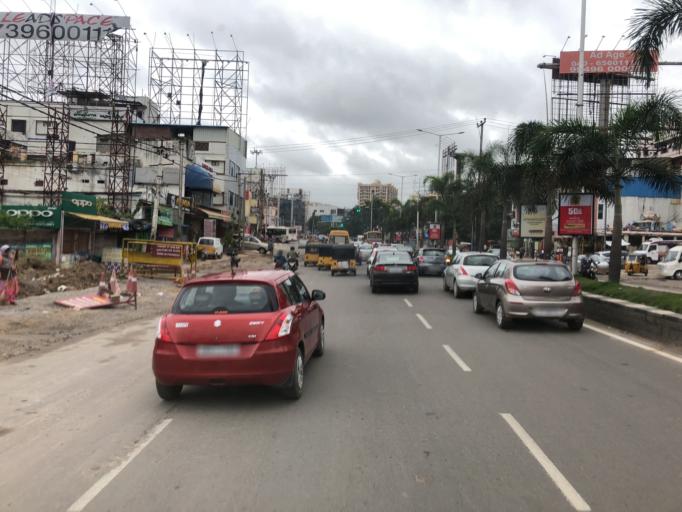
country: IN
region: Telangana
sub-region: Rangareddi
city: Kukatpalli
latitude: 17.4602
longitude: 78.3665
